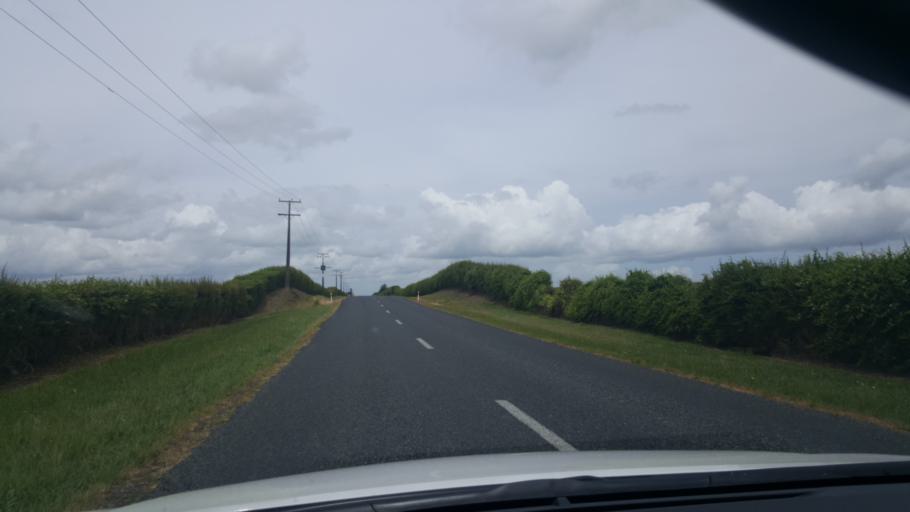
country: NZ
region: Waikato
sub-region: Matamata-Piako District
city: Matamata
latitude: -37.8774
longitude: 175.7278
